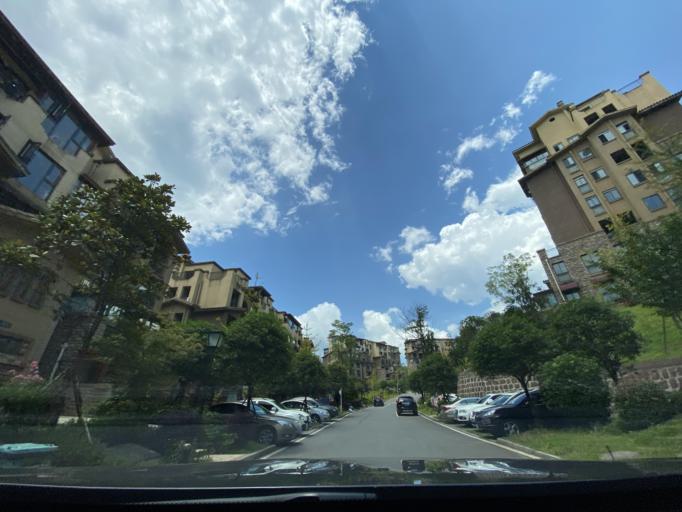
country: CN
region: Guizhou Sheng
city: Changqi
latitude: 28.5354
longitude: 105.9734
